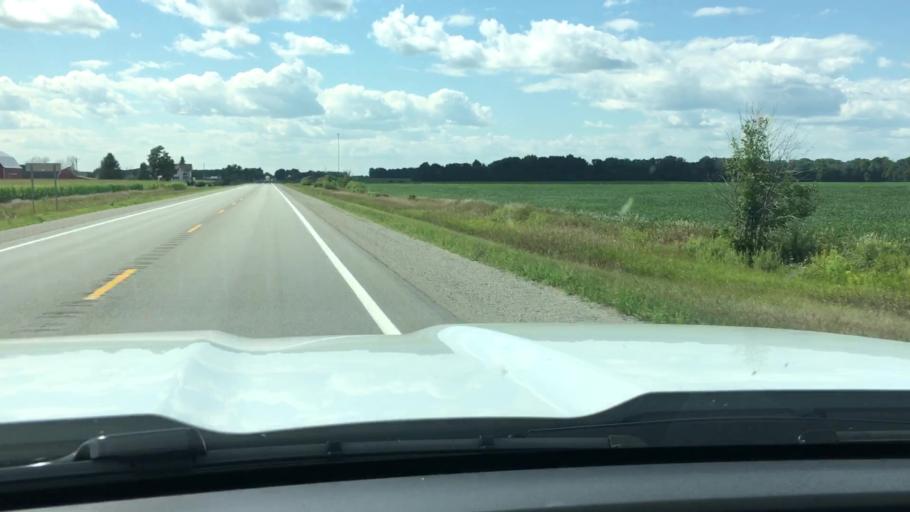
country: US
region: Michigan
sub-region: Montcalm County
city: Carson City
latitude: 43.1766
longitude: -84.7806
